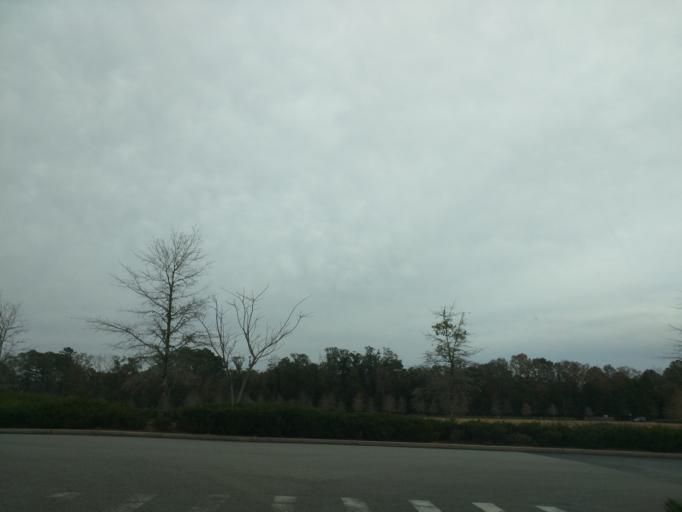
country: US
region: Florida
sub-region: Leon County
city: Tallahassee
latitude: 30.4619
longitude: -84.2118
